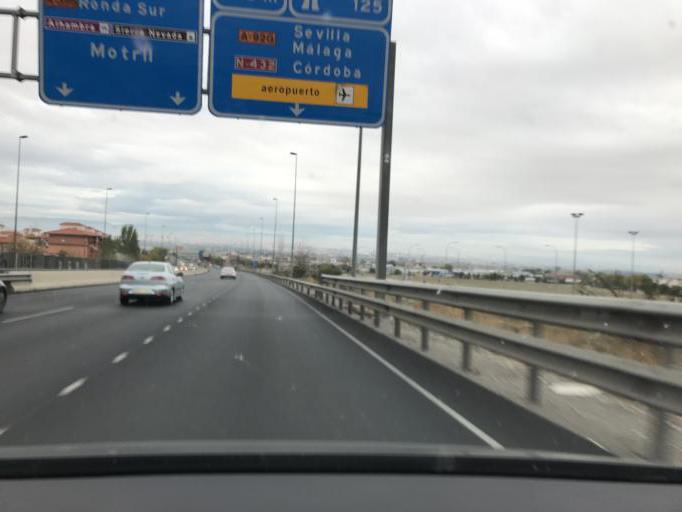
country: ES
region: Andalusia
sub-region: Provincia de Granada
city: Maracena
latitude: 37.2031
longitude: -3.6281
